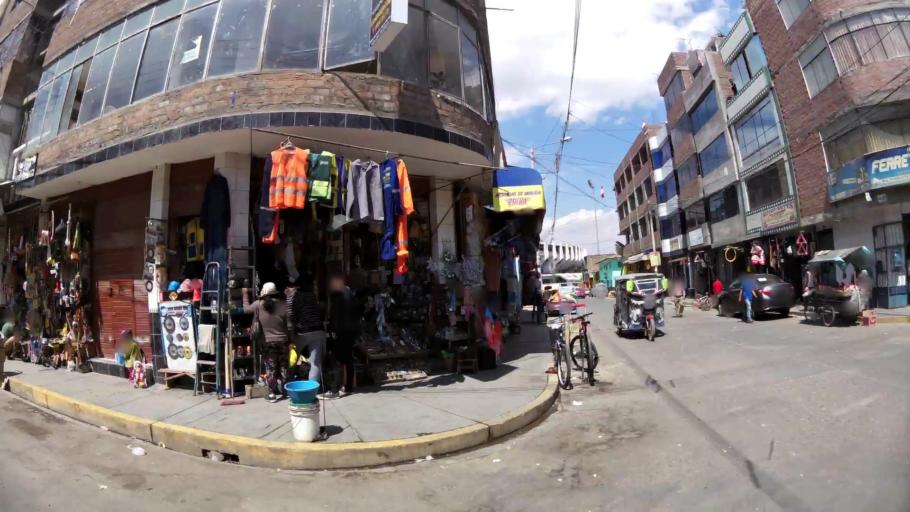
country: PE
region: Junin
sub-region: Provincia de Huancayo
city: Huancayo
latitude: -12.0710
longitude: -75.2030
